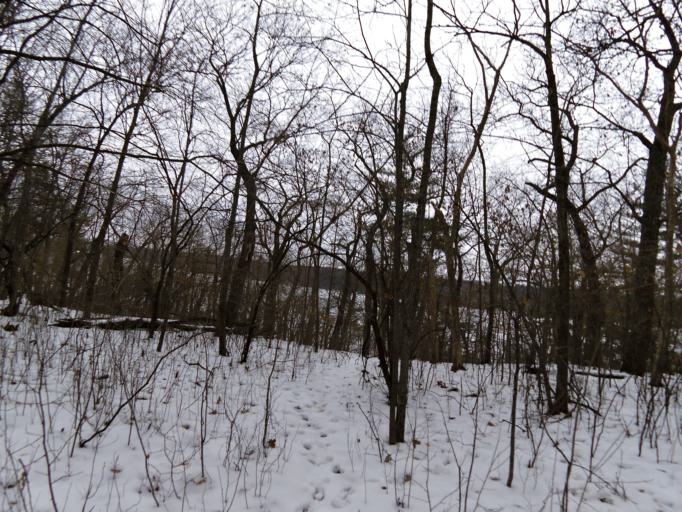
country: US
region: Wisconsin
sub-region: Pierce County
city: Prescott
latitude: 44.8052
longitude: -92.7877
